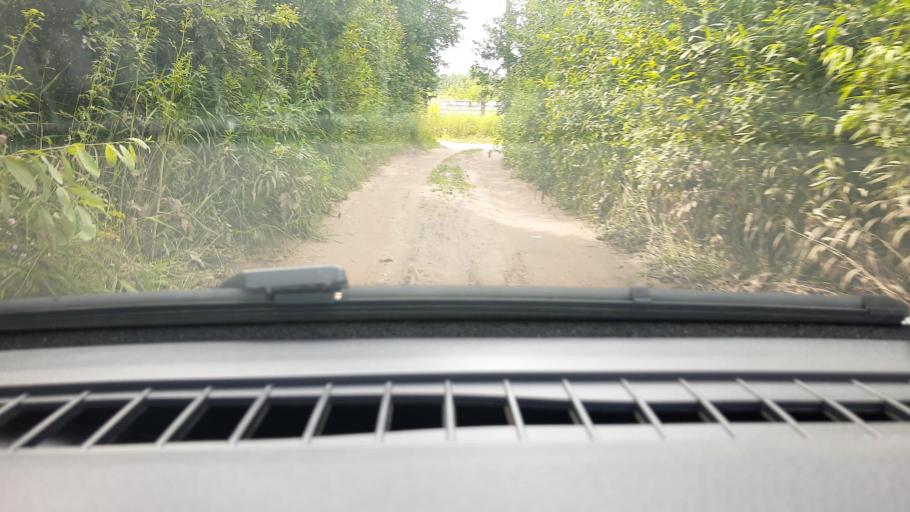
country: RU
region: Nizjnij Novgorod
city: Neklyudovo
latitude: 56.4277
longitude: 44.0038
